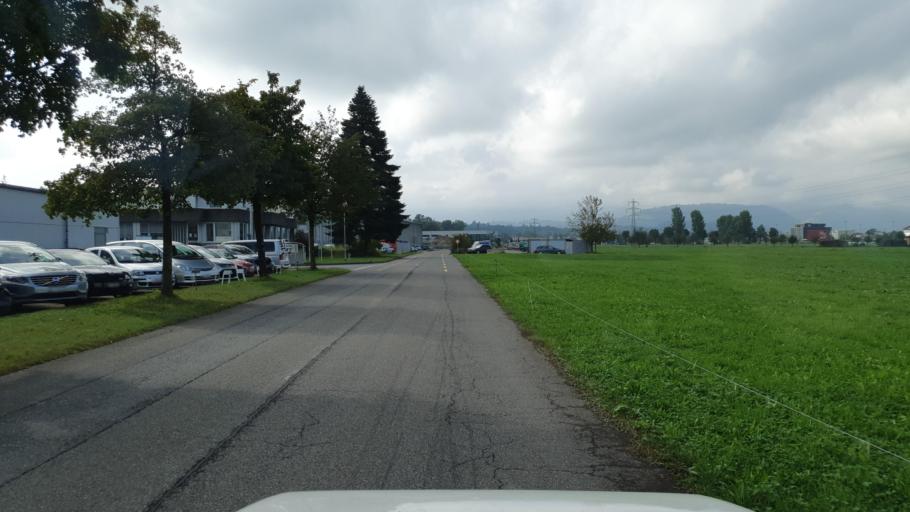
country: CH
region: Lucerne
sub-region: Lucerne-Land District
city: Ebikon
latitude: 47.0919
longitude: 8.3178
